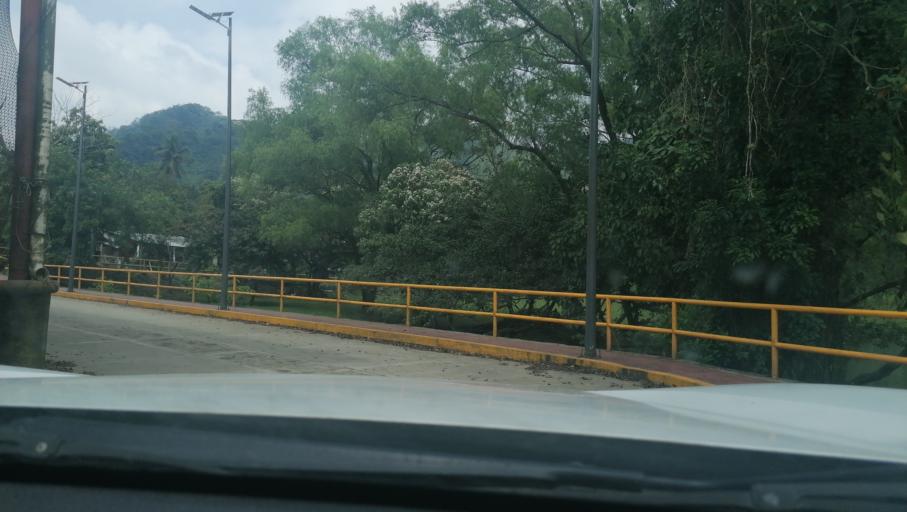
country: MX
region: Chiapas
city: Ostuacan
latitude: 17.3638
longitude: -93.3267
